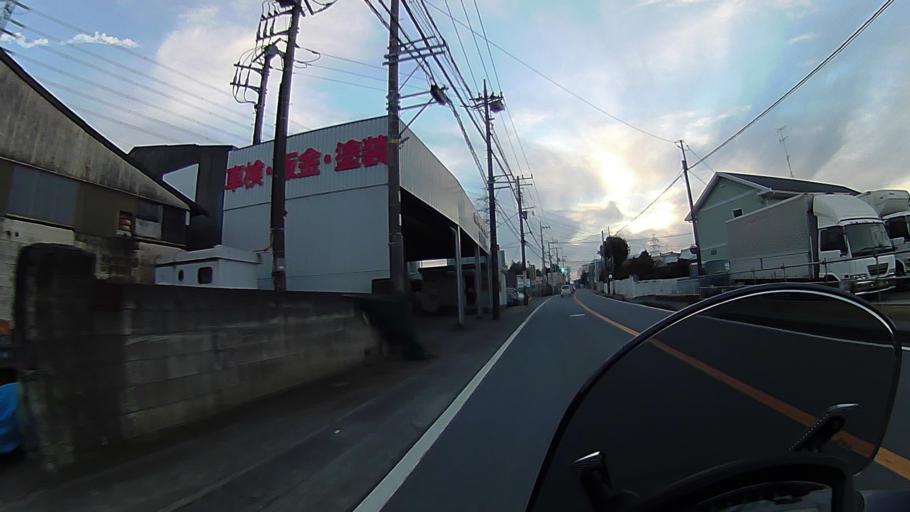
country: JP
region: Kanagawa
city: Minami-rinkan
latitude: 35.4222
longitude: 139.4258
